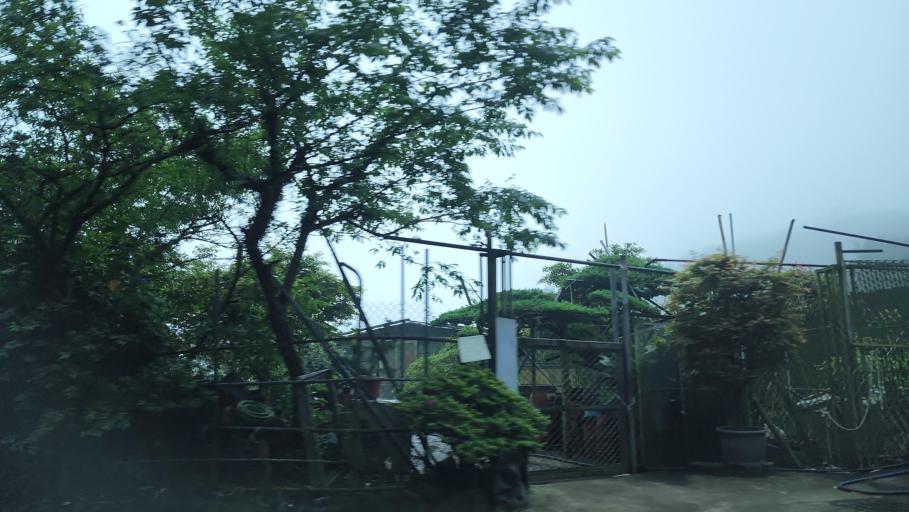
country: TW
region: Taipei
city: Taipei
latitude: 25.1461
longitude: 121.6036
